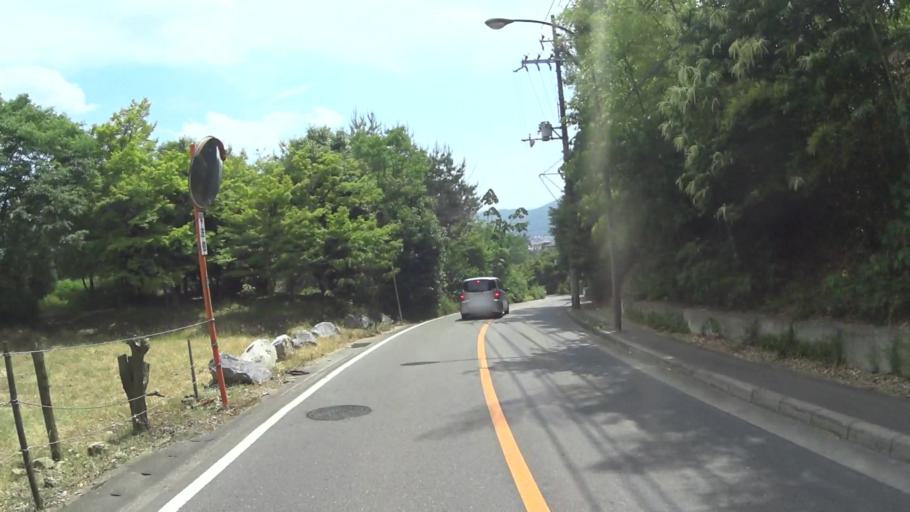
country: JP
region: Kyoto
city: Kyoto
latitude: 35.0284
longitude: 135.6960
